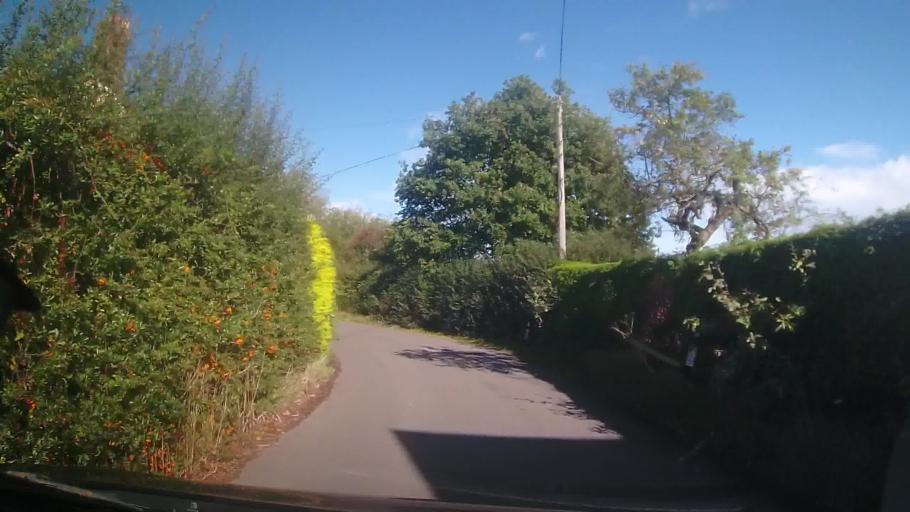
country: GB
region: England
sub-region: Shropshire
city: Wem
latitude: 52.8465
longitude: -2.7045
